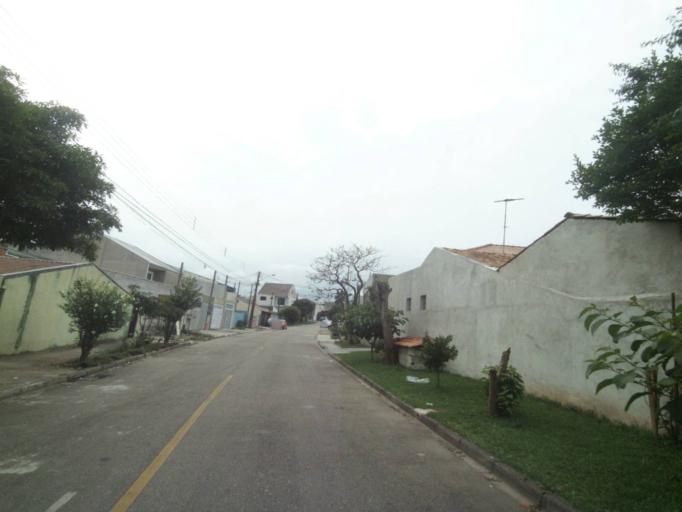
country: BR
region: Parana
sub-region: Sao Jose Dos Pinhais
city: Sao Jose dos Pinhais
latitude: -25.5497
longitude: -49.2684
